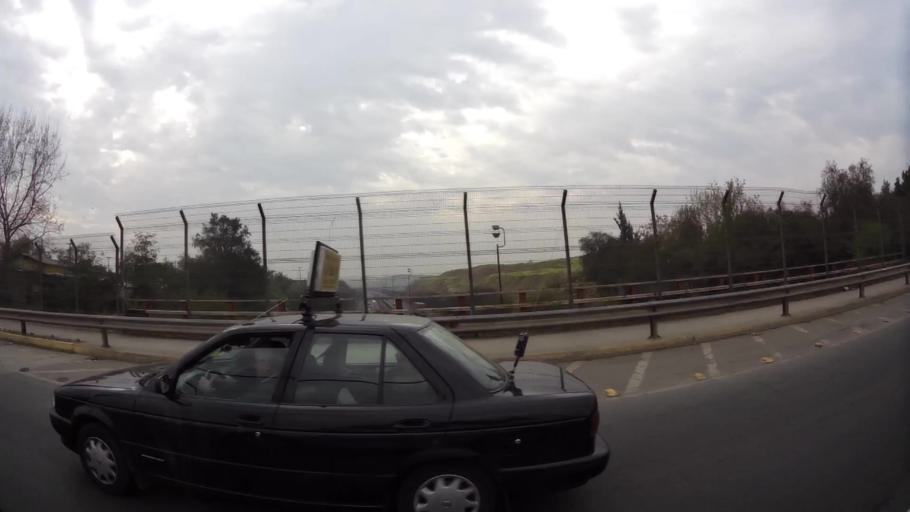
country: CL
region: Santiago Metropolitan
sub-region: Provincia de Santiago
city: Lo Prado
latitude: -33.4838
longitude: -70.7246
